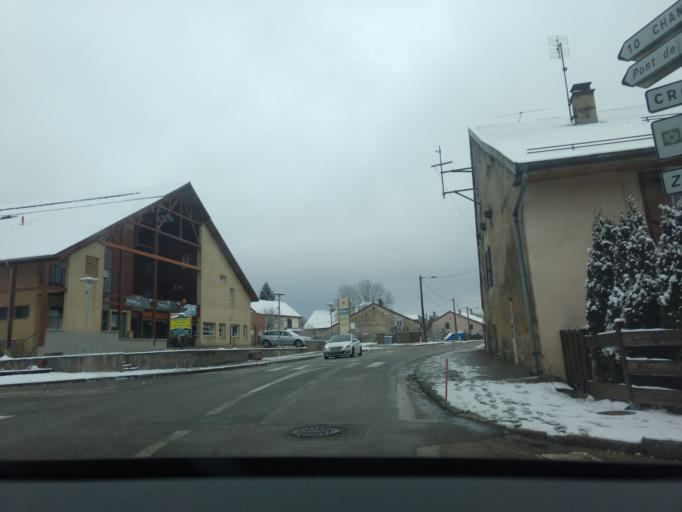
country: FR
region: Franche-Comte
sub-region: Departement du Jura
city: Champagnole
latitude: 46.7947
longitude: 5.8372
